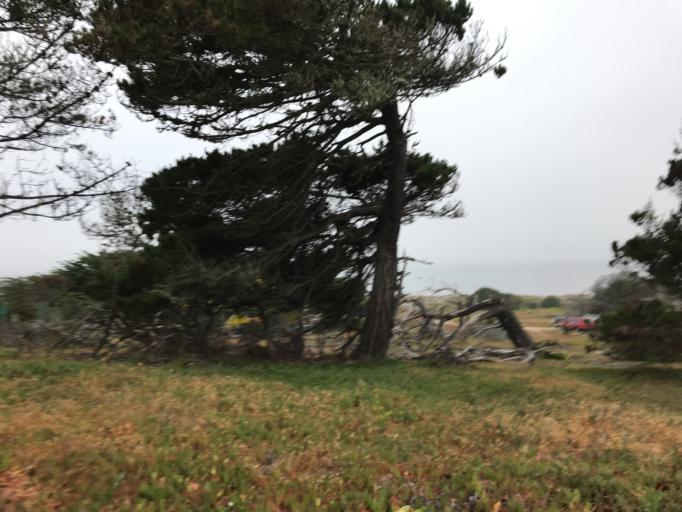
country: US
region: California
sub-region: Monterey County
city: Pacific Grove
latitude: 36.6289
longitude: -121.9351
